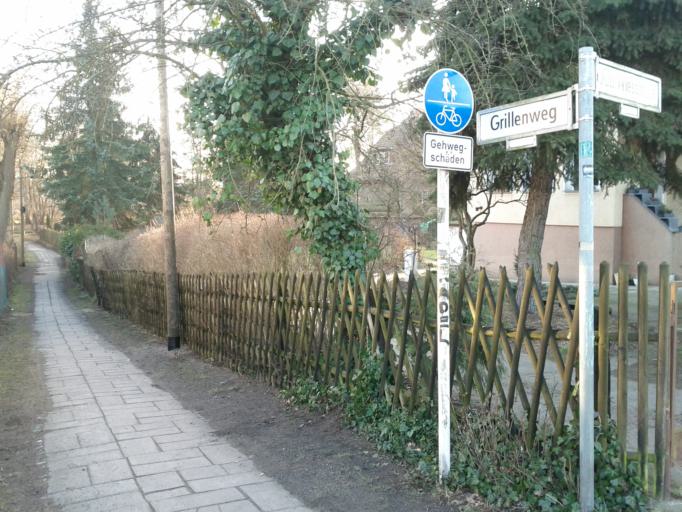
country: DE
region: Berlin
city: Friedrichshagen
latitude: 52.4577
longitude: 13.6040
